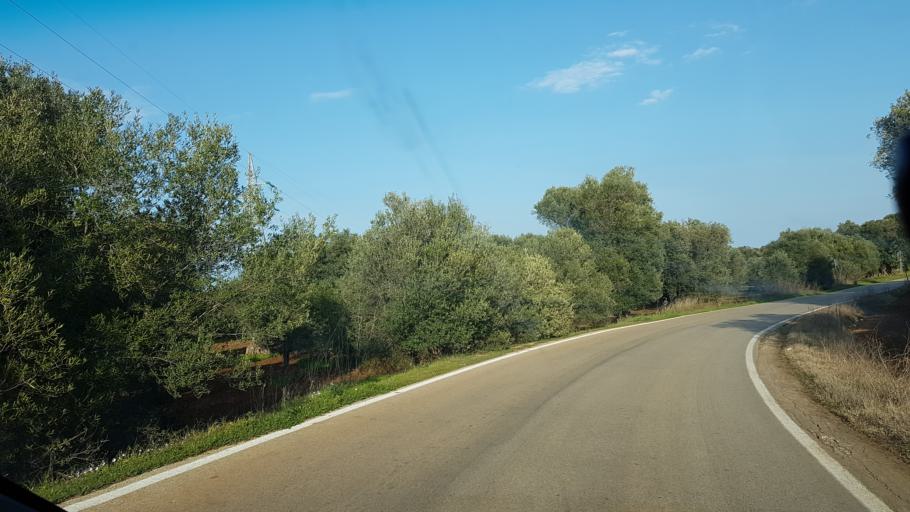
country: IT
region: Apulia
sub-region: Provincia di Brindisi
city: San Vito dei Normanni
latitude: 40.7005
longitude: 17.7604
